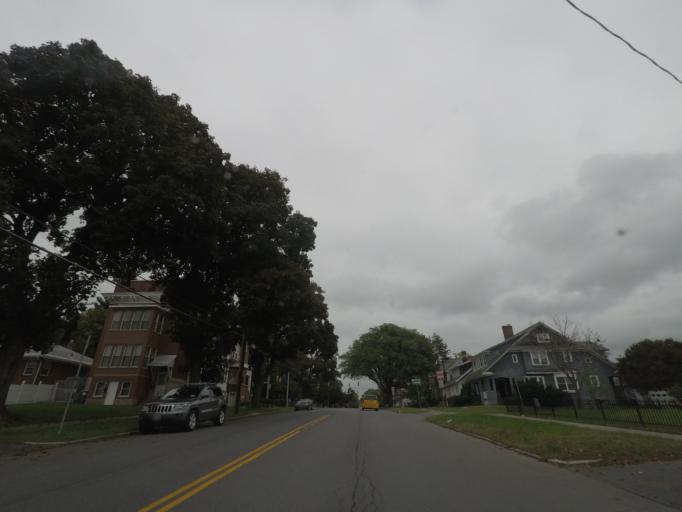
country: US
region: New York
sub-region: Albany County
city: West Albany
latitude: 42.6692
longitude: -73.7840
